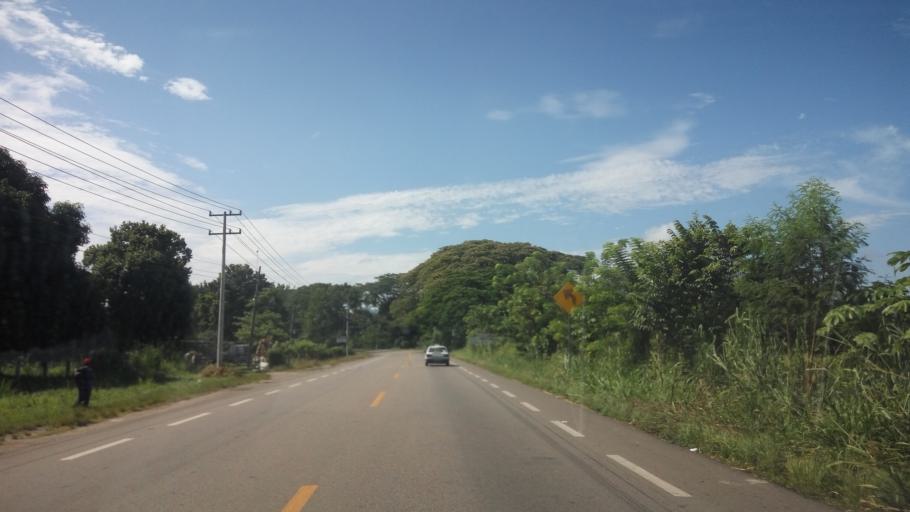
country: MX
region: Tabasco
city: Teapa
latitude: 17.5847
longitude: -92.9678
